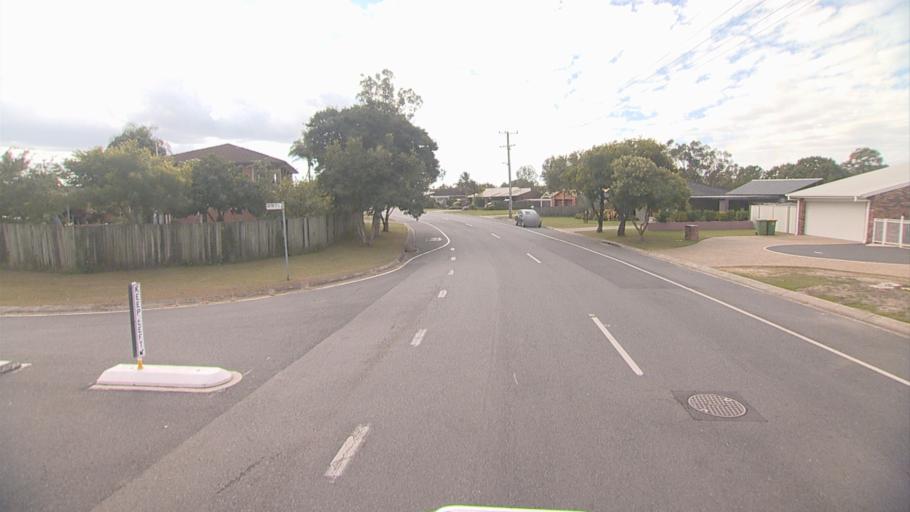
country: AU
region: Queensland
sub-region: Logan
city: Windaroo
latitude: -27.7317
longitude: 153.2122
